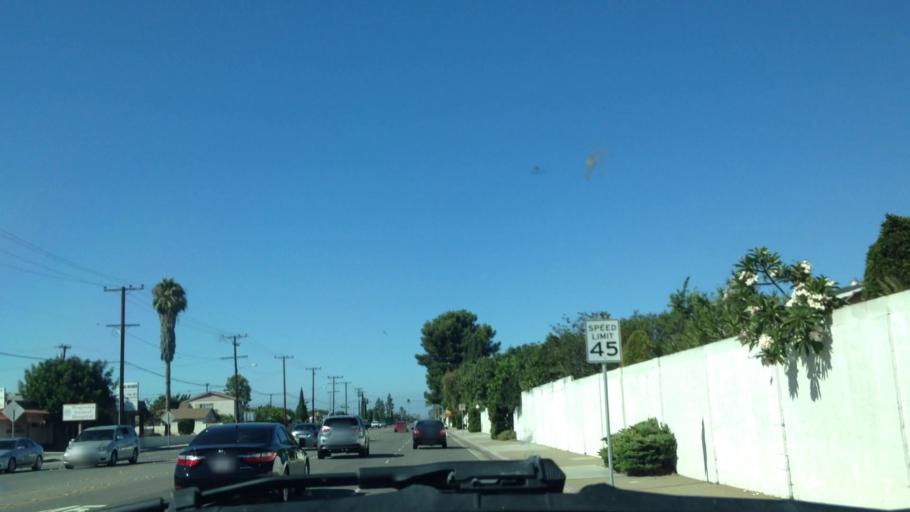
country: US
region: California
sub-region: Orange County
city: Fountain Valley
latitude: 33.7235
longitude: -117.9719
